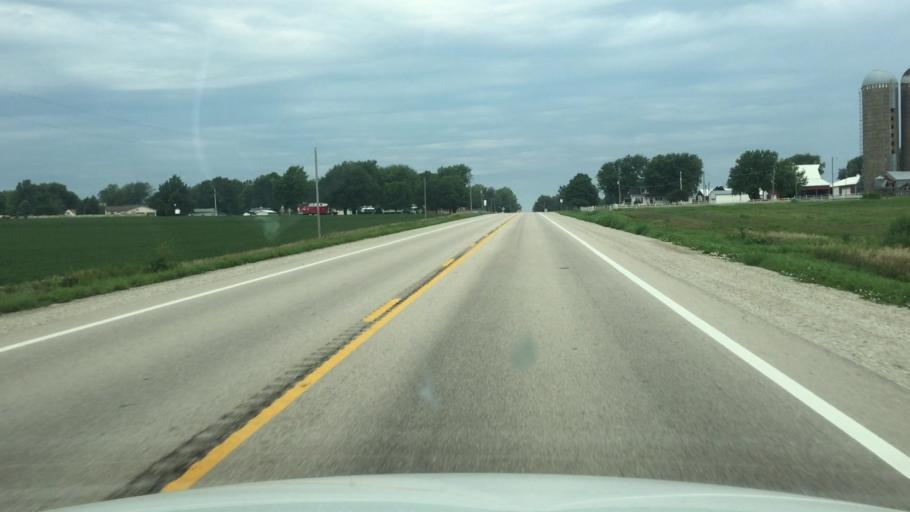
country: US
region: Kansas
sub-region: Nemaha County
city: Sabetha
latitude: 39.8412
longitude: -95.7183
